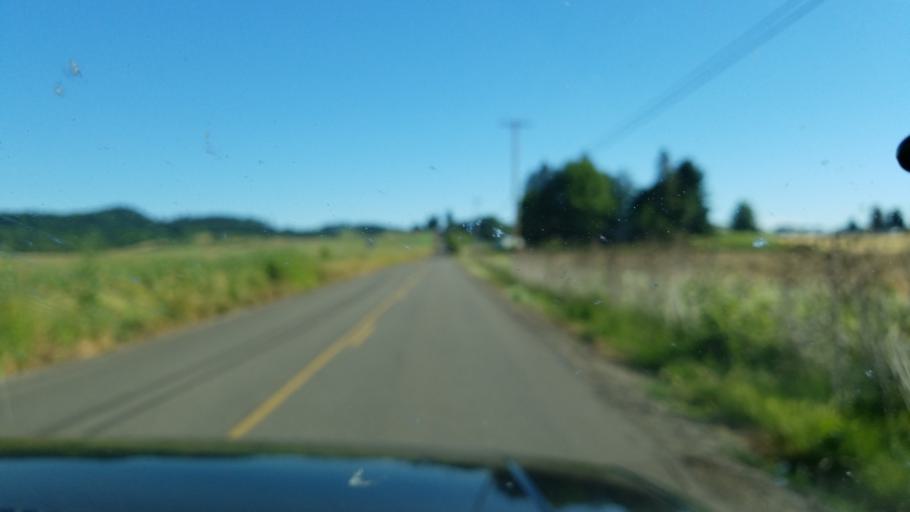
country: US
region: Oregon
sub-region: Yamhill County
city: McMinnville
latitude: 45.2316
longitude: -123.2310
